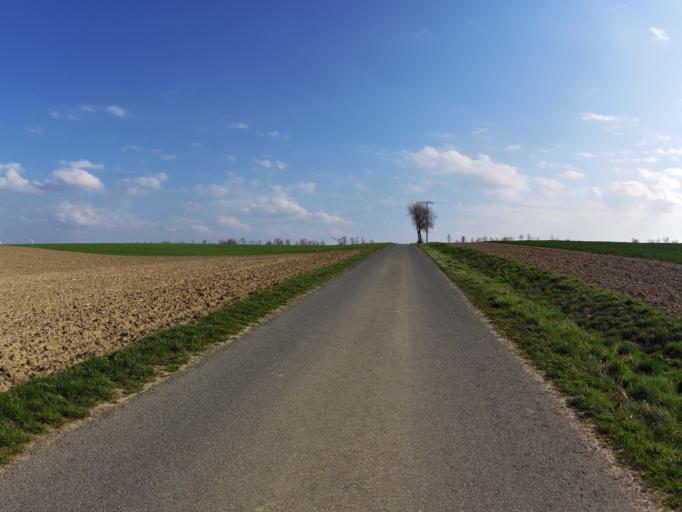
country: DE
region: Bavaria
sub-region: Regierungsbezirk Unterfranken
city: Biebelried
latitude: 49.7887
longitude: 10.0852
